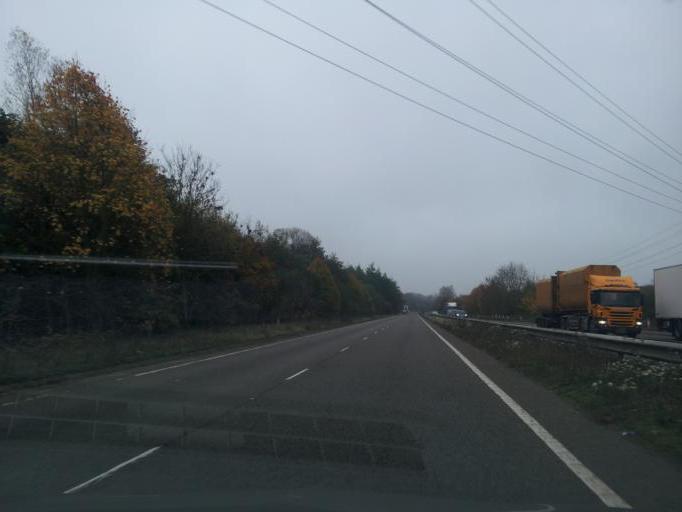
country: GB
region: England
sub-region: Northamptonshire
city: Brackley
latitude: 52.0352
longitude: -1.1342
